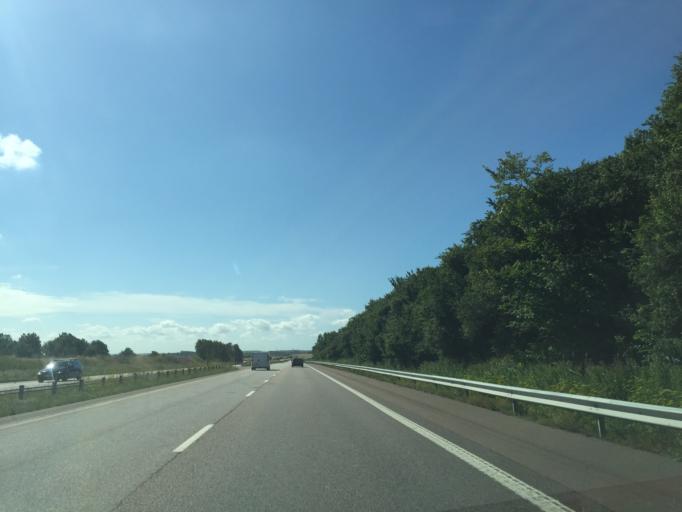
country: SE
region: Skane
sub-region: Angelholms Kommun
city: Strovelstorp
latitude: 56.1543
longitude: 12.8438
